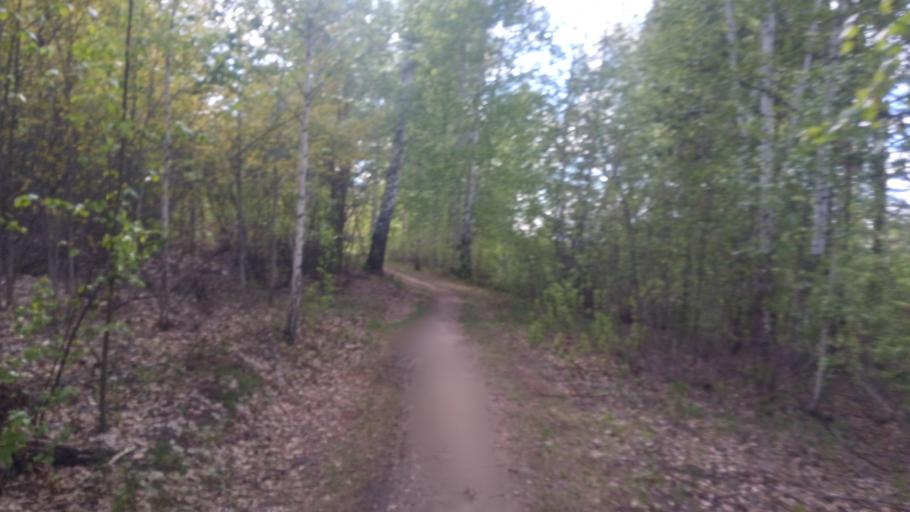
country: RU
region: Chelyabinsk
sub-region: Gorod Chelyabinsk
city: Chelyabinsk
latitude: 55.1678
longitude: 61.3240
